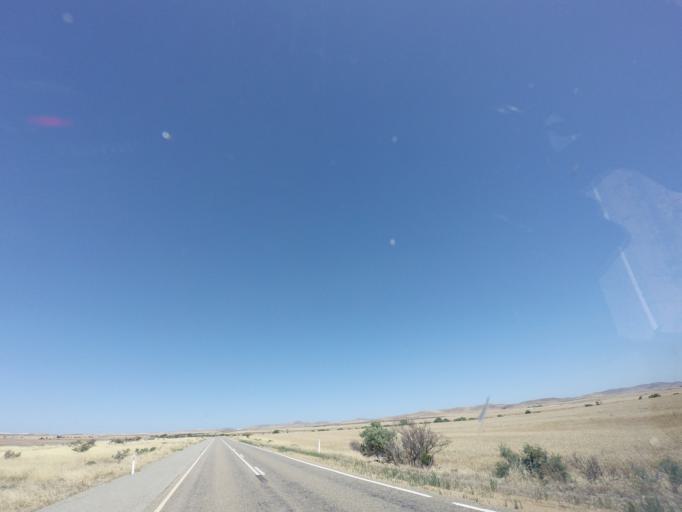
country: AU
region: South Australia
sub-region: Peterborough
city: Peterborough
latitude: -32.7133
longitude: 138.4504
